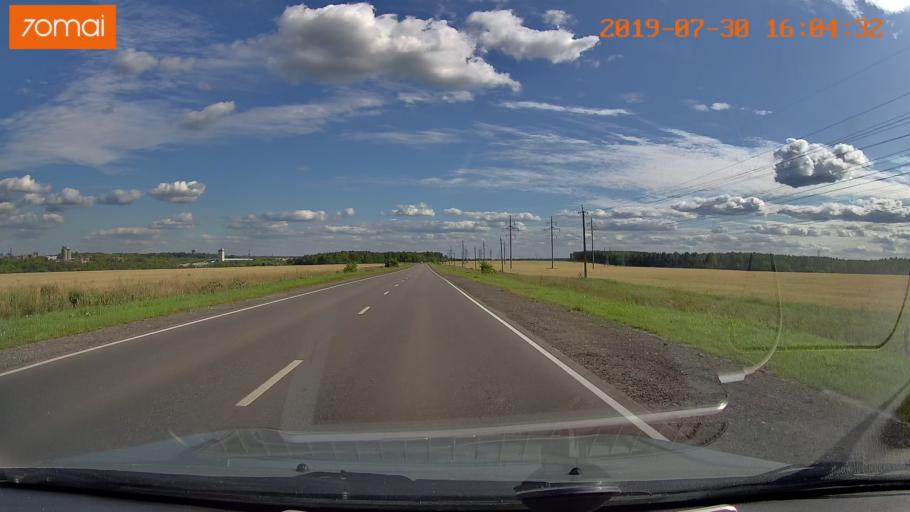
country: RU
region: Moskovskaya
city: Lopatinskiy
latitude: 55.2796
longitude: 38.7082
